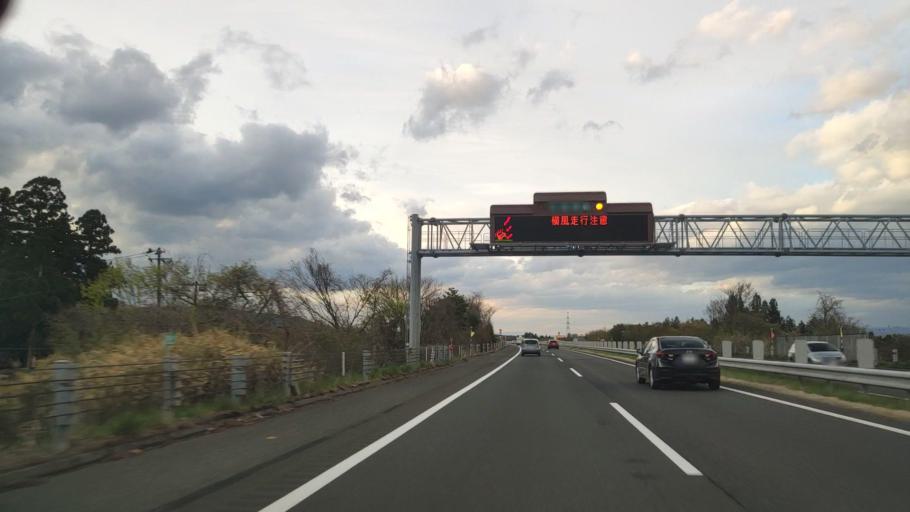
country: JP
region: Iwate
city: Morioka-shi
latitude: 39.5703
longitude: 141.1204
